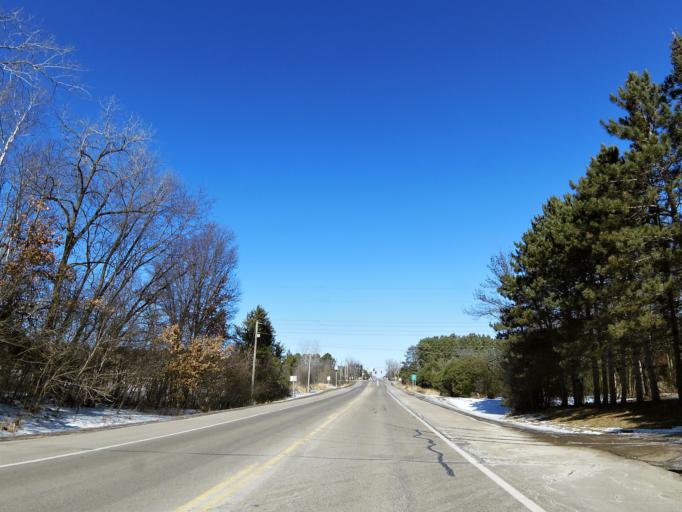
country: US
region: Minnesota
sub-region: Washington County
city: Lake Elmo
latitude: 45.0331
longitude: -92.8834
